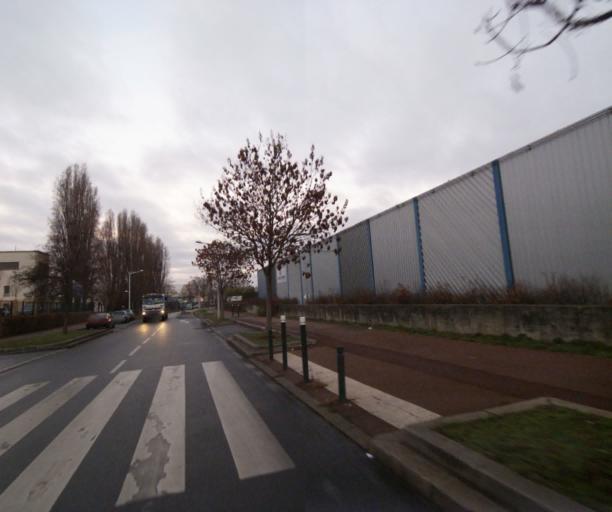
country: FR
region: Ile-de-France
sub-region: Departement des Yvelines
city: Carrieres-sur-Seine
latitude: 48.8964
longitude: 2.1808
